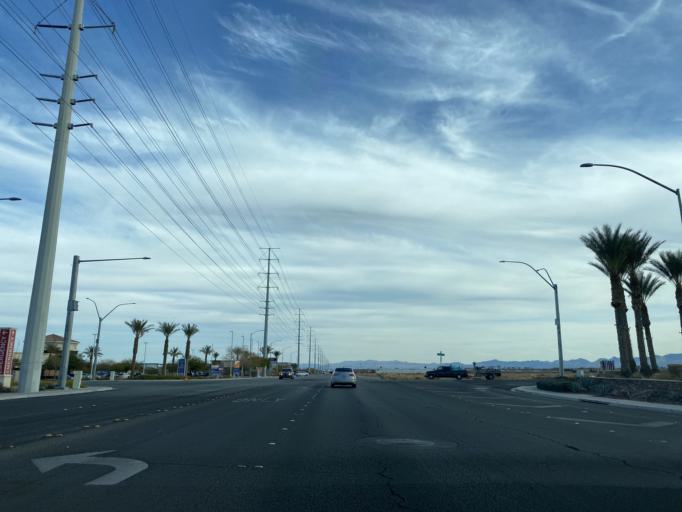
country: US
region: Nevada
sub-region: Clark County
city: Enterprise
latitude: 36.0555
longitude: -115.2711
